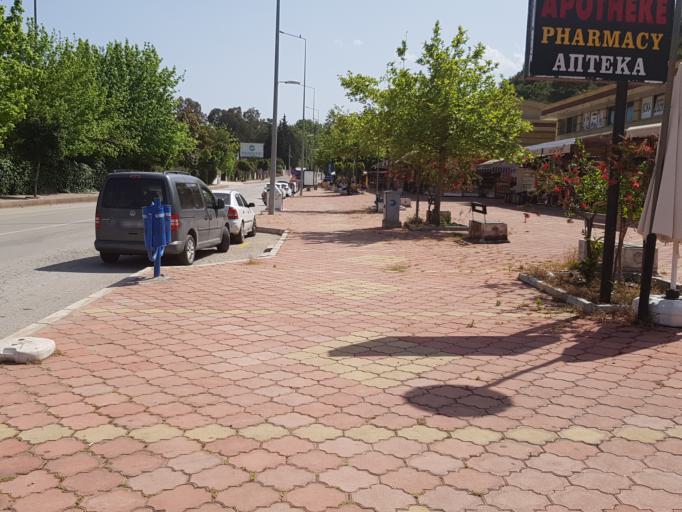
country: TR
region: Antalya
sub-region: Kemer
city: Goeynuek
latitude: 36.6559
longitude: 30.5547
